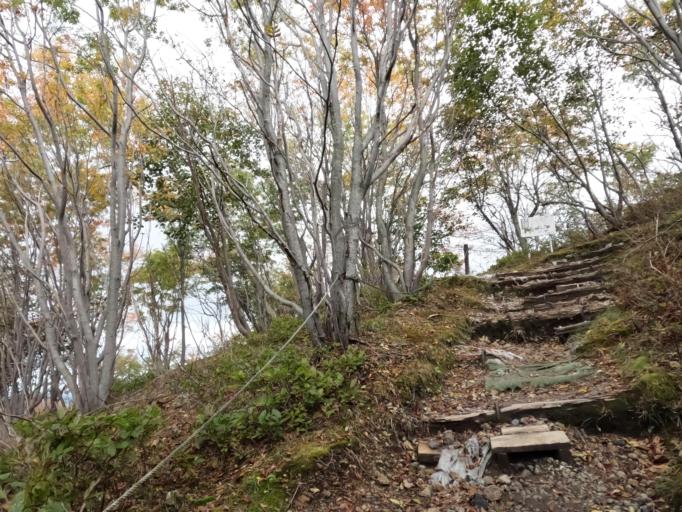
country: JP
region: Hokkaido
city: Shiraoi
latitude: 42.6989
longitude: 141.3911
